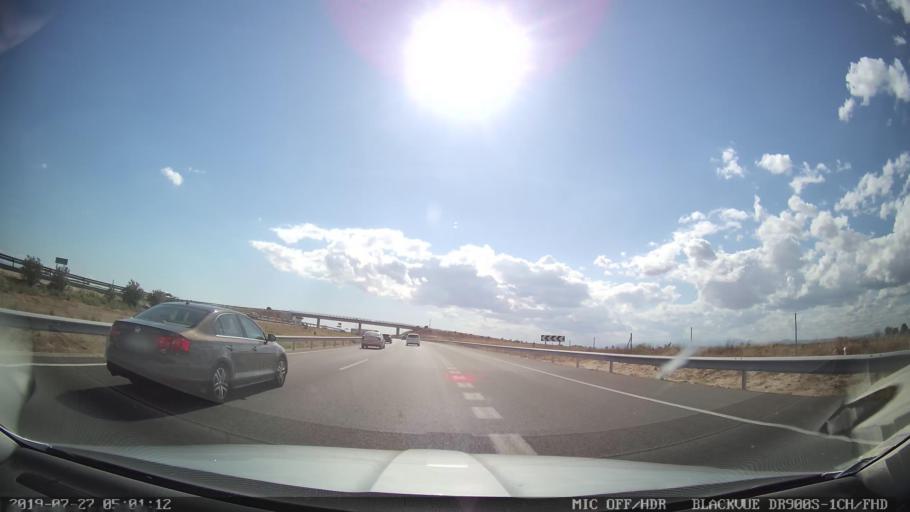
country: ES
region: Castille-La Mancha
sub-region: Province of Toledo
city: Las Ventas de Retamosa
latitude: 40.1877
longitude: -4.1252
